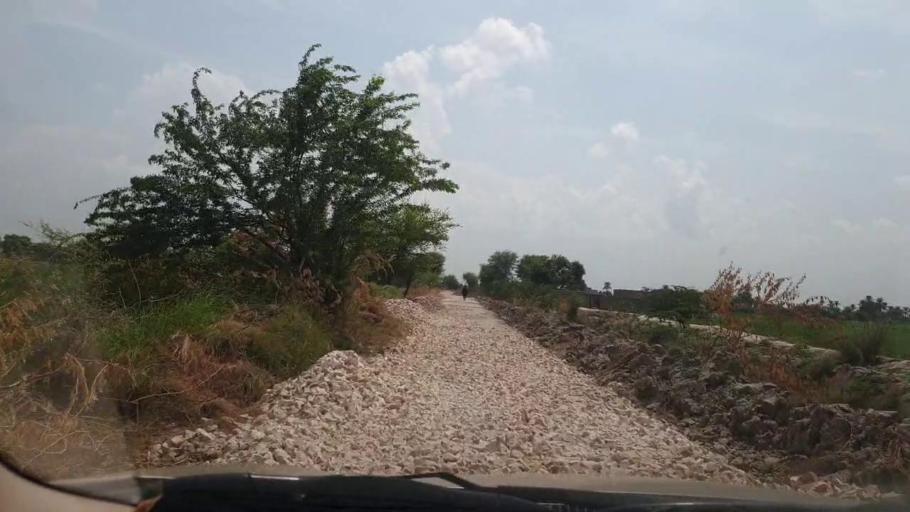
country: PK
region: Sindh
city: Larkana
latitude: 27.5647
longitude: 68.1096
